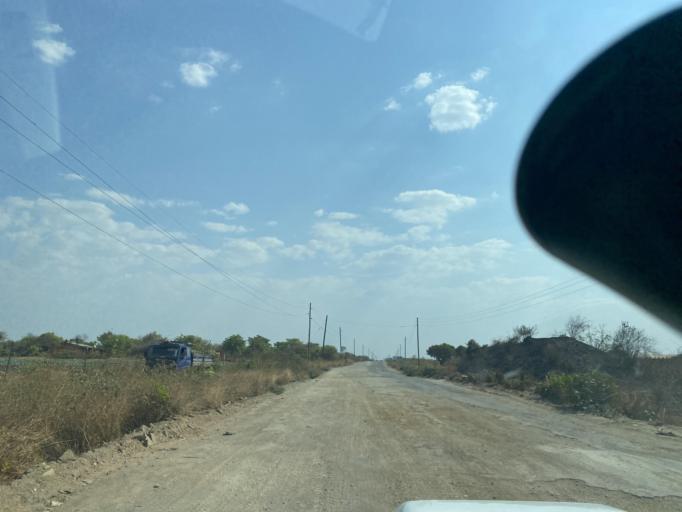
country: ZM
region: Lusaka
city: Lusaka
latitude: -15.3517
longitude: 28.1080
